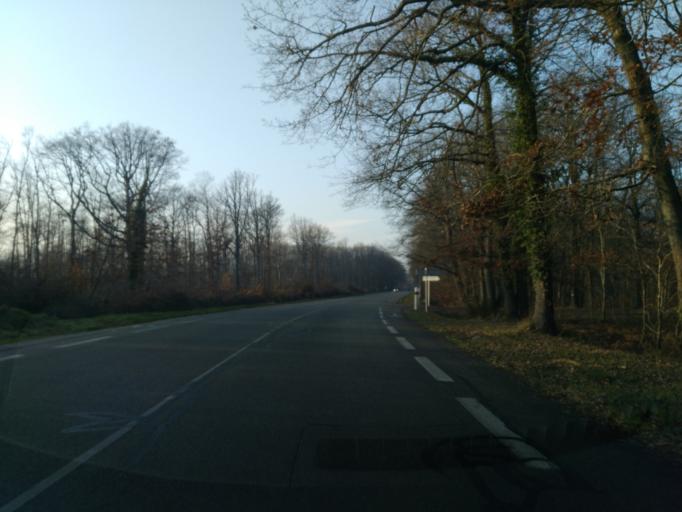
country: FR
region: Ile-de-France
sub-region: Departement des Yvelines
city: Neauphle-le-Chateau
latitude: 48.8001
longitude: 1.9203
